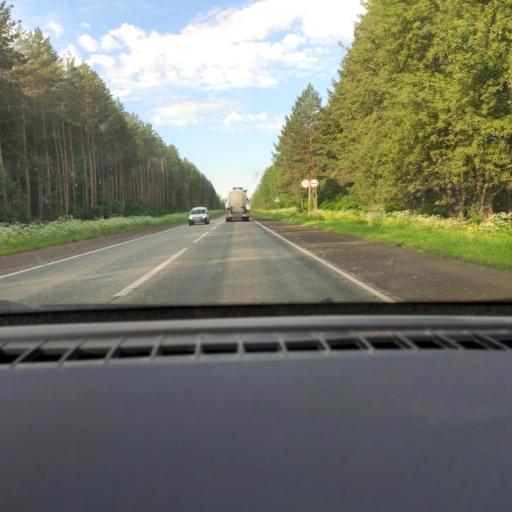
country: RU
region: Udmurtiya
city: Votkinsk
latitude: 57.0259
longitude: 53.9157
